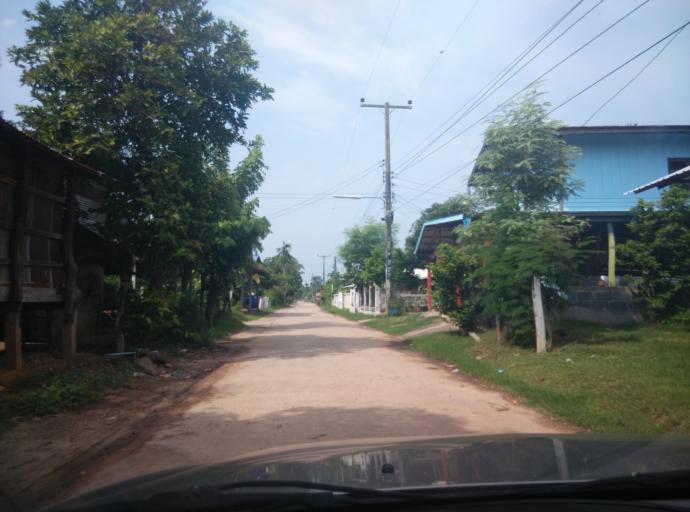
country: TH
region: Sisaket
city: Huai Thap Than
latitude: 15.0517
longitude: 104.0831
